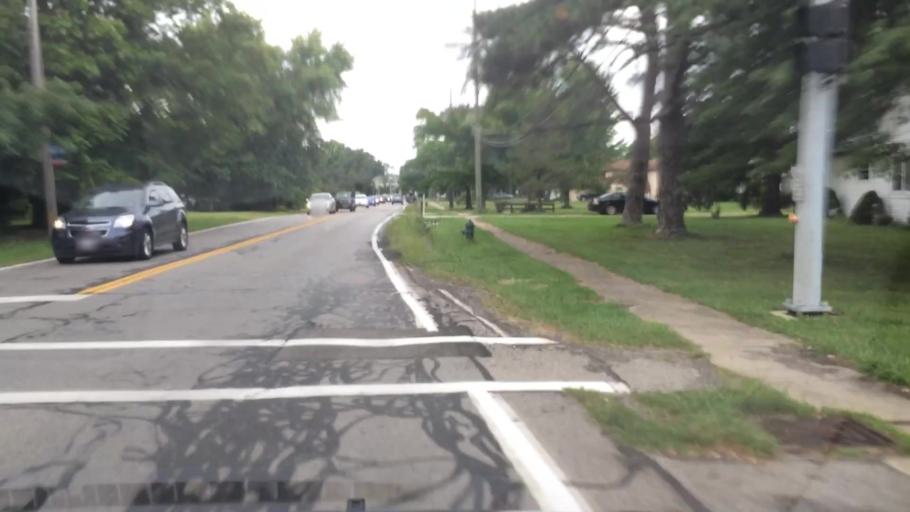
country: US
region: Ohio
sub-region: Cuyahoga County
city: Strongsville
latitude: 41.3018
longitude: -81.8109
